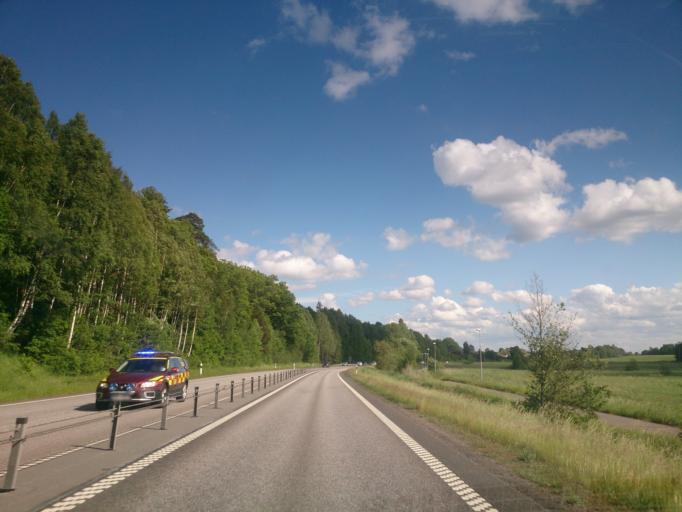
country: SE
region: OEstergoetland
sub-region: Norrkopings Kommun
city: Jursla
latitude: 58.6710
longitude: 16.1604
